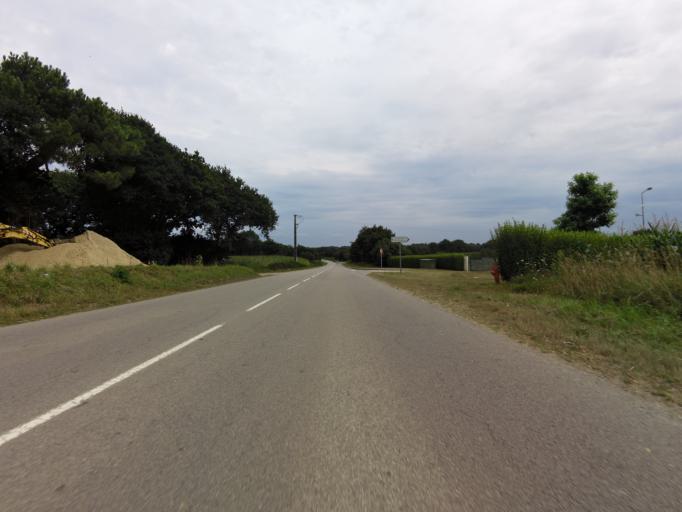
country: FR
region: Brittany
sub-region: Departement du Finistere
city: Poullan-sur-Mer
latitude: 48.0852
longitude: -4.3851
